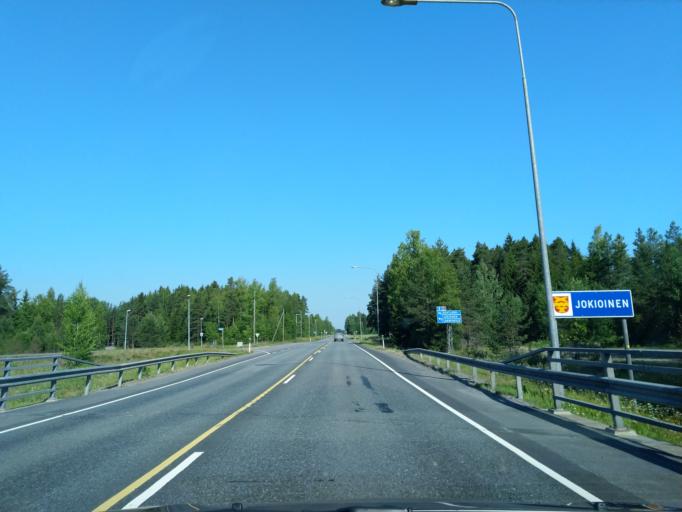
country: FI
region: Haeme
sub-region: Forssa
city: Forssa
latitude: 60.8308
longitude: 23.5621
